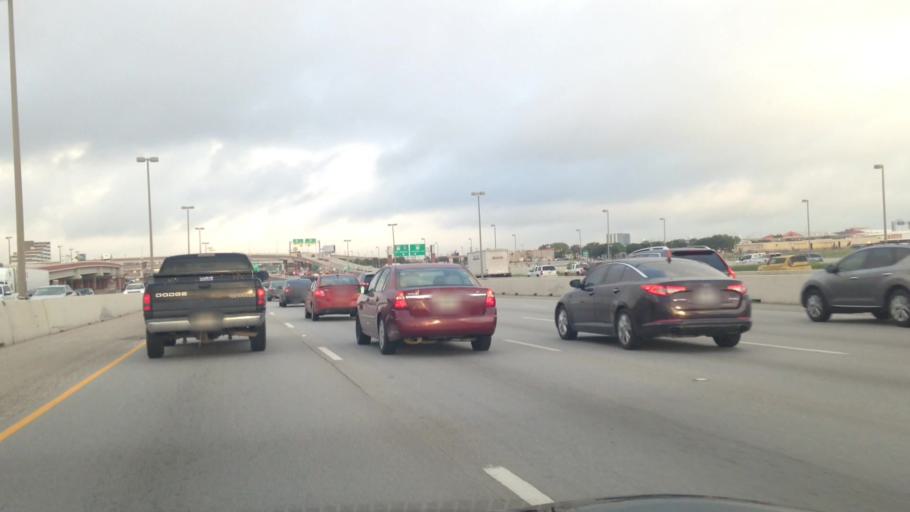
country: US
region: Texas
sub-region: Bexar County
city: Alamo Heights
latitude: 29.5189
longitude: -98.4718
